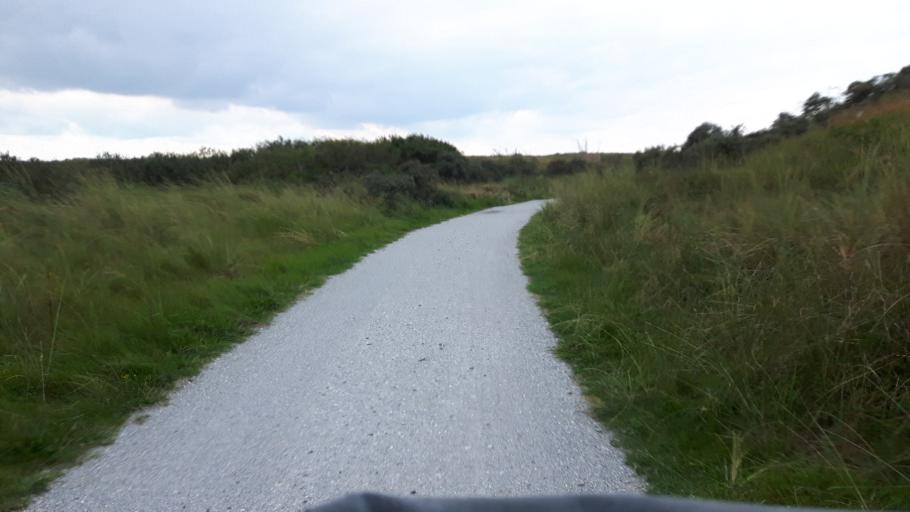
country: NL
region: Friesland
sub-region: Gemeente Ameland
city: Nes
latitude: 53.4590
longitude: 5.8325
